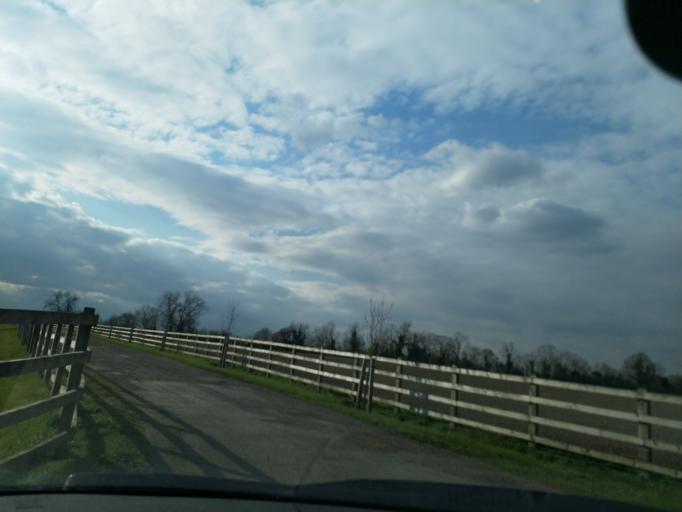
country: GB
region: England
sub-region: Warwickshire
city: Harbury
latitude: 52.2122
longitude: -1.5199
